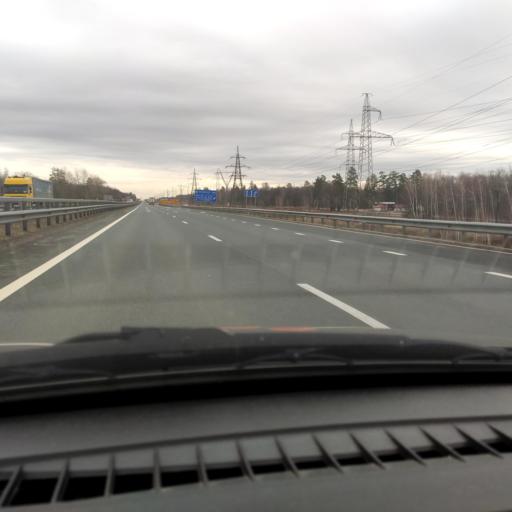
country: RU
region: Samara
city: Pribrezhnyy
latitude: 53.5176
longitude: 49.8361
